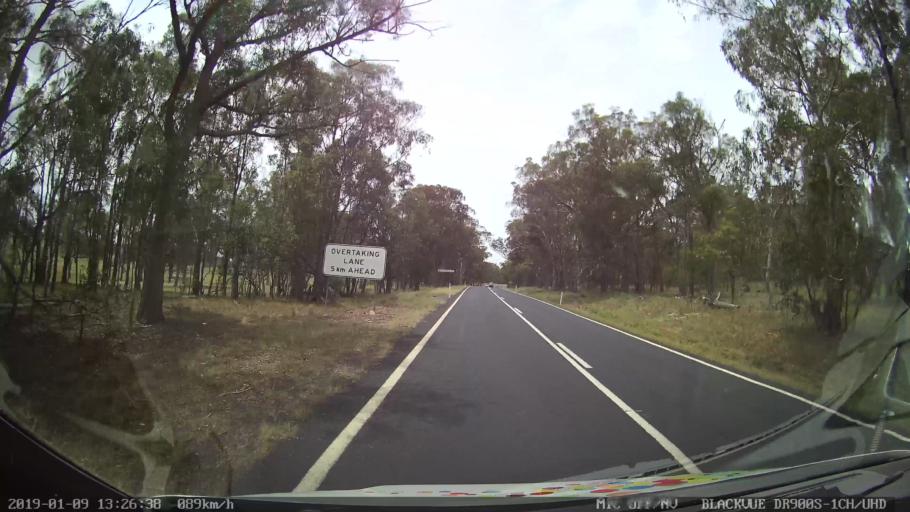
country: AU
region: New South Wales
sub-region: Armidale Dumaresq
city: Enmore
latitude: -30.5252
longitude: 151.9447
